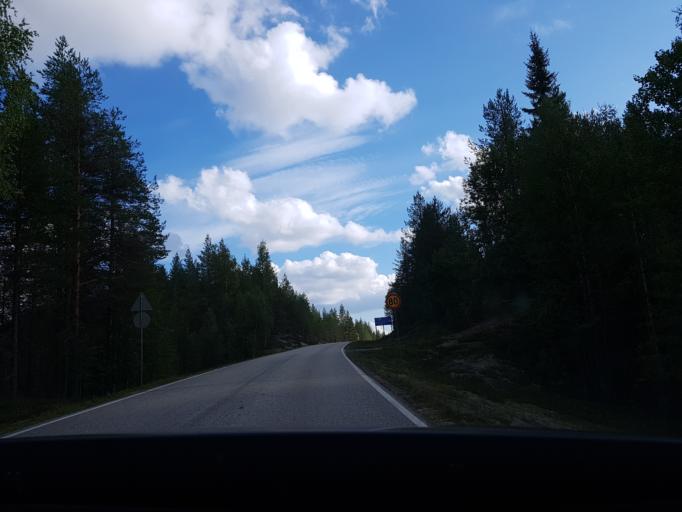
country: FI
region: Kainuu
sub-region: Kehys-Kainuu
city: Kuhmo
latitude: 64.6253
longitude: 29.6972
